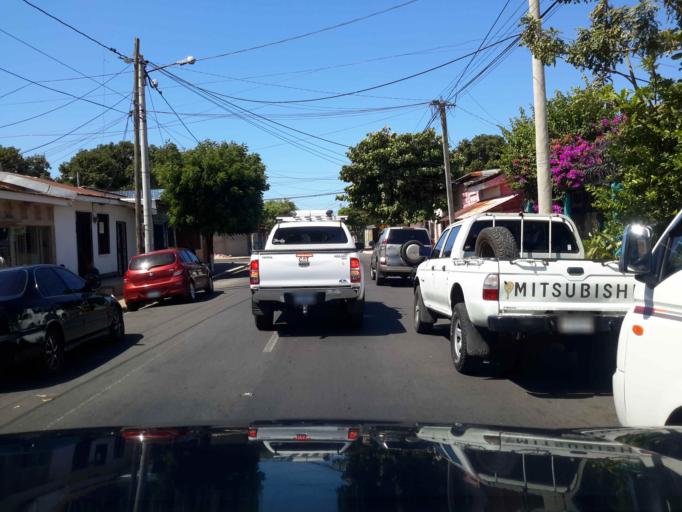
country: NI
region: Managua
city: Managua
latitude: 12.1501
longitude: -86.2959
